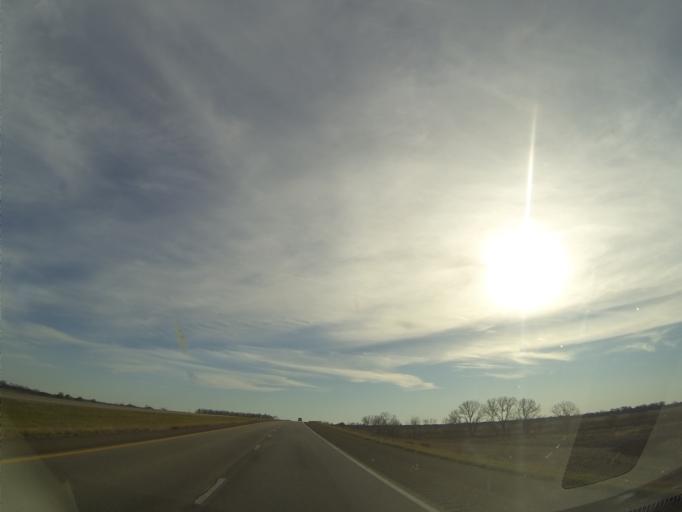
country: US
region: Kansas
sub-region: Ottawa County
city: Minneapolis
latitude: 39.0740
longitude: -97.6495
